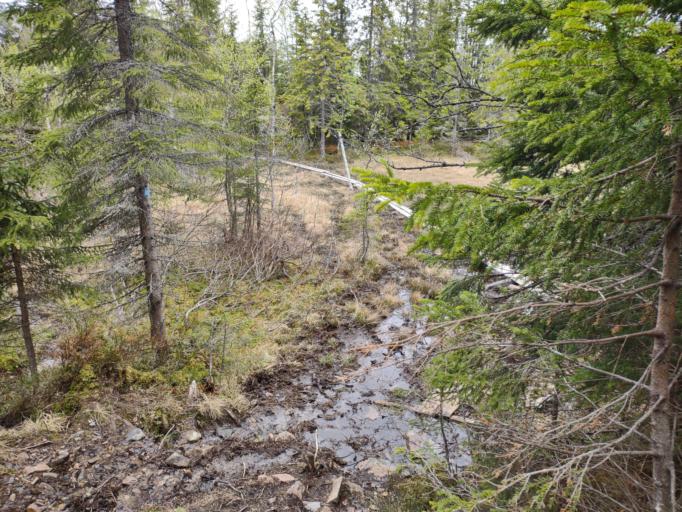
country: NO
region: Oppland
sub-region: Gran
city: Jaren
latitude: 60.4312
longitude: 10.6818
